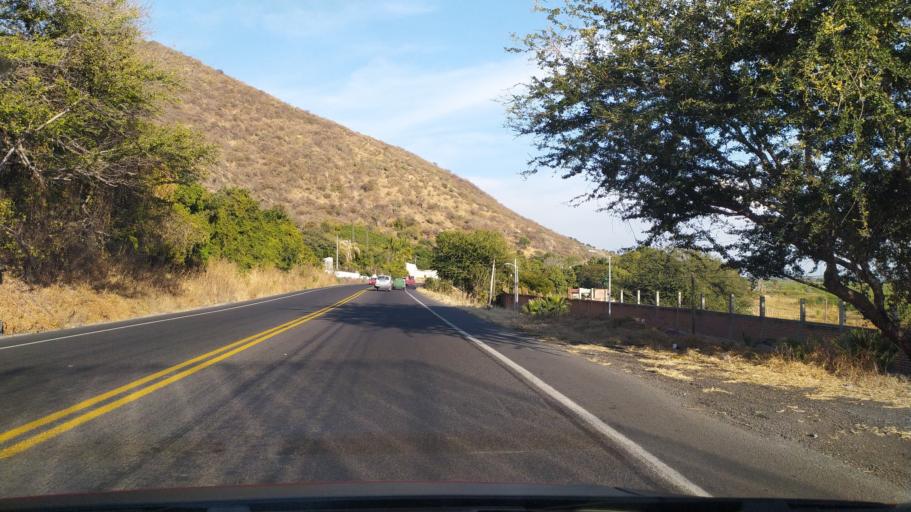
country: MX
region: Jalisco
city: Jamay
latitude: 20.2941
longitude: -102.7383
